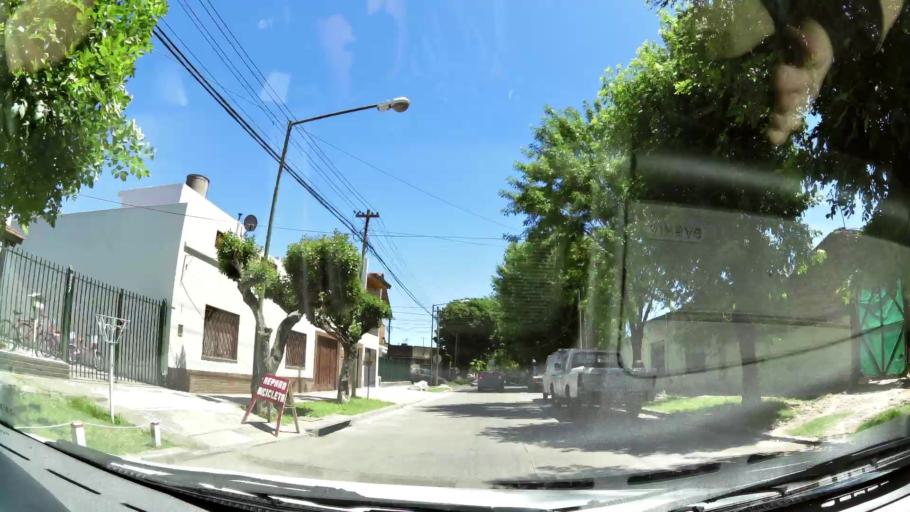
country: AR
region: Buenos Aires
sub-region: Partido de San Isidro
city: San Isidro
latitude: -34.5092
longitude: -58.5548
